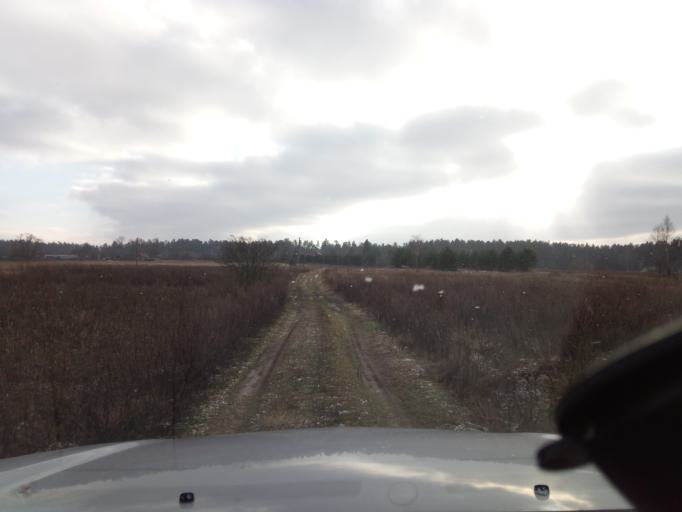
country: LT
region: Alytaus apskritis
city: Druskininkai
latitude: 54.1149
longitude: 24.2189
